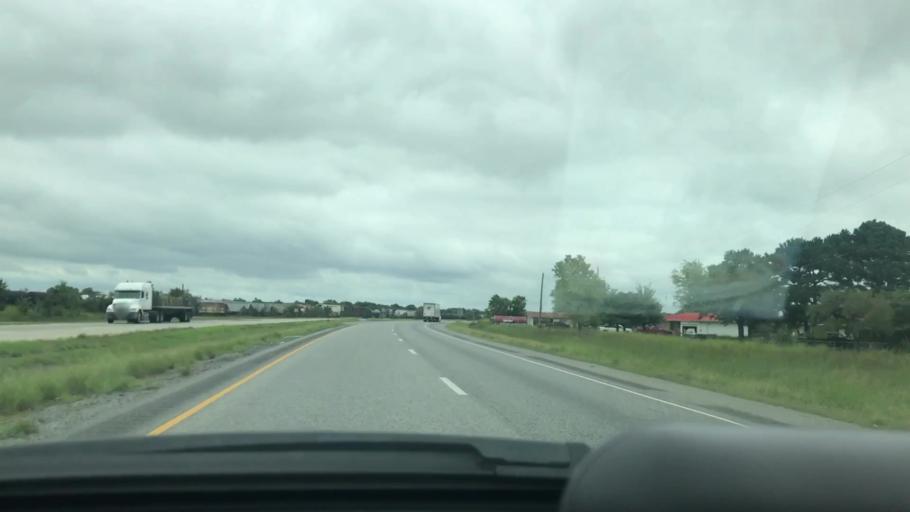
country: US
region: Oklahoma
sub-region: Pittsburg County
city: McAlester
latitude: 34.7346
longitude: -95.8996
